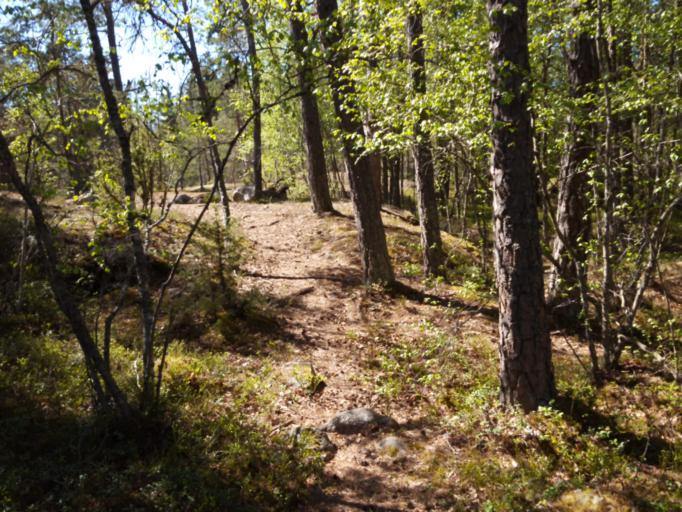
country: SE
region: Uppsala
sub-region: Uppsala Kommun
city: Storvreta
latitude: 59.9046
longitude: 17.7499
